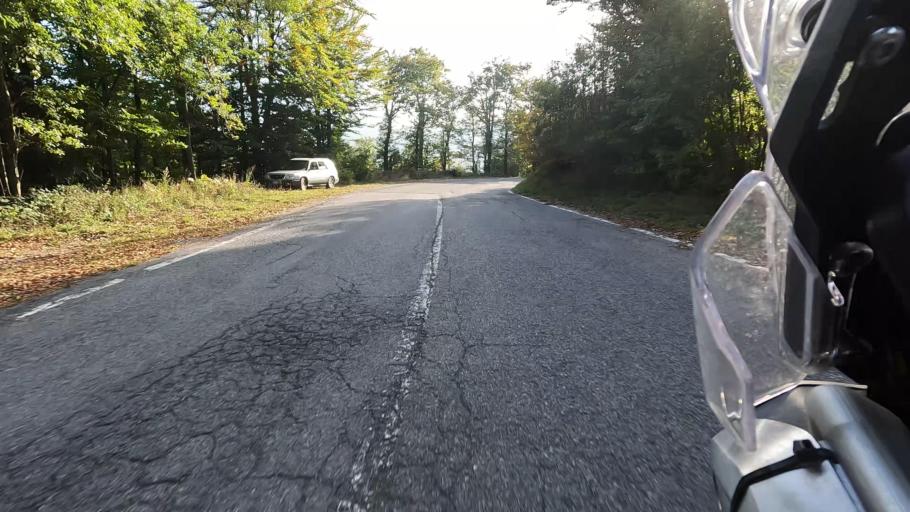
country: IT
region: Liguria
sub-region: Provincia di Savona
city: Urbe
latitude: 44.4658
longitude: 8.5535
